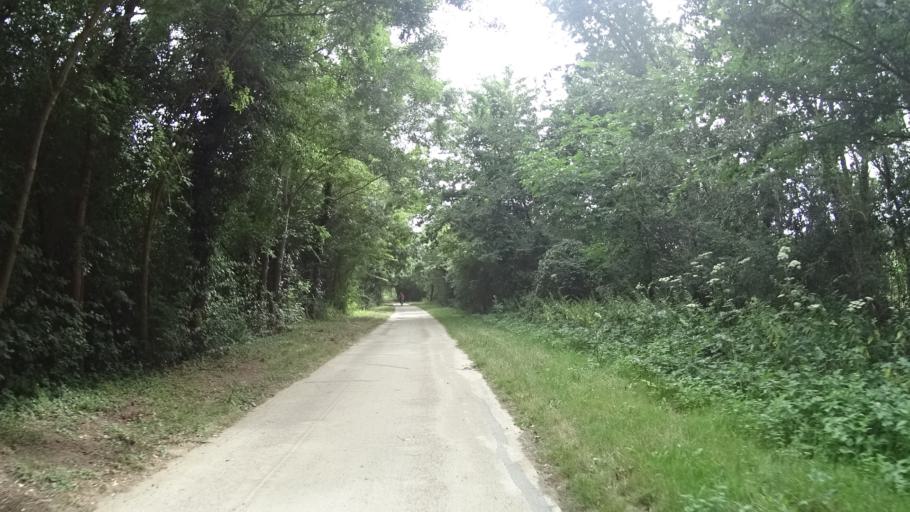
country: FR
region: Centre
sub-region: Departement d'Indre-et-Loire
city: Huismes
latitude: 47.2475
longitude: 0.2420
